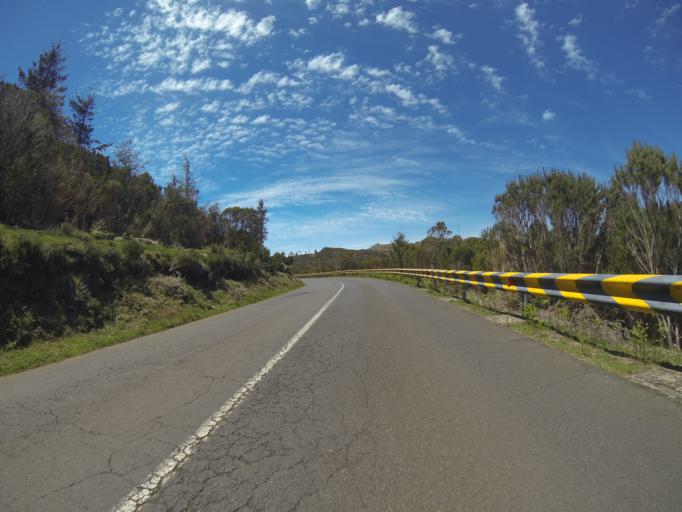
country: PT
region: Madeira
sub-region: Funchal
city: Nossa Senhora do Monte
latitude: 32.7132
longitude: -16.8992
